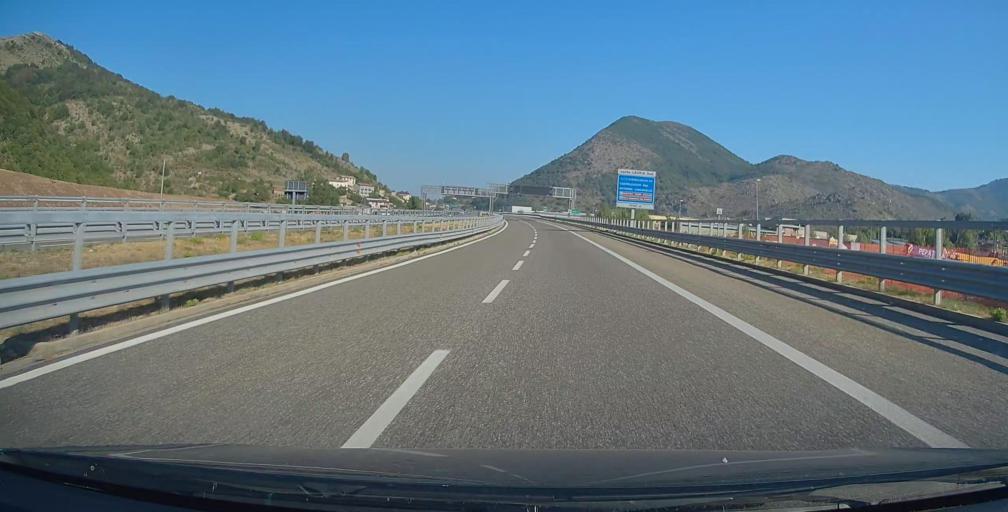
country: IT
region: Basilicate
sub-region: Provincia di Potenza
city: Lauria
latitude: 40.0121
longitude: 15.9003
